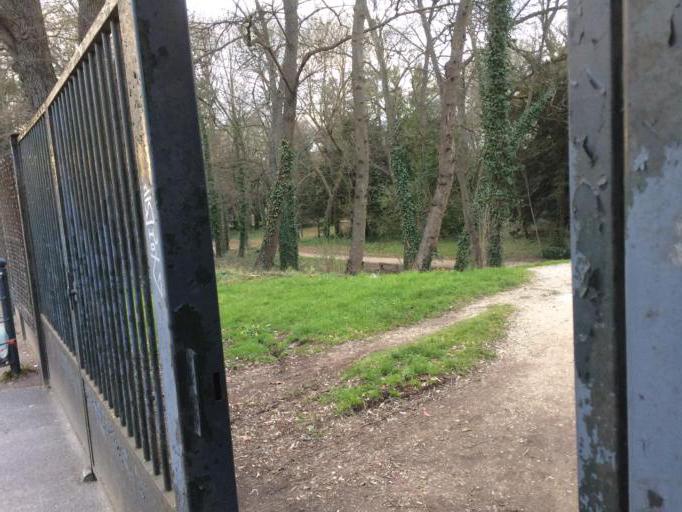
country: FR
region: Ile-de-France
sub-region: Departement de l'Essonne
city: Grigny
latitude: 48.6523
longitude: 2.3982
